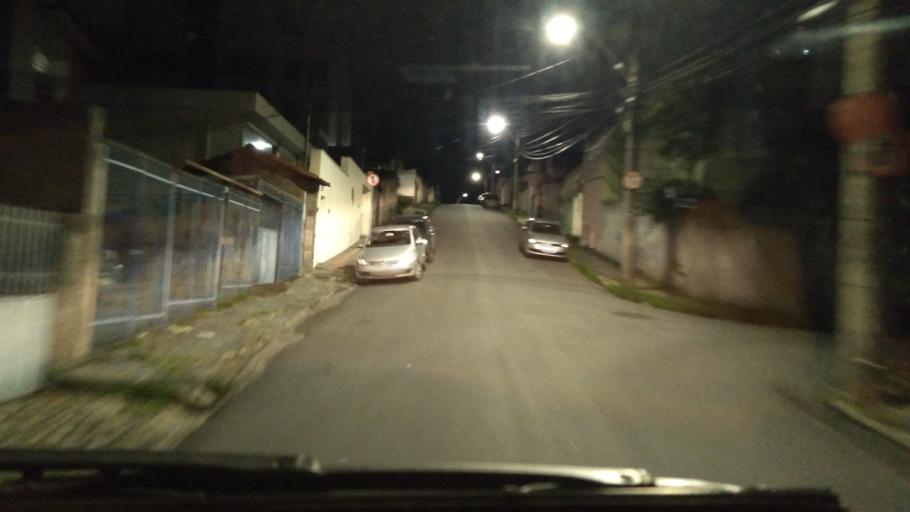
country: BR
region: Minas Gerais
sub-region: Belo Horizonte
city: Belo Horizonte
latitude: -19.8974
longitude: -43.9700
